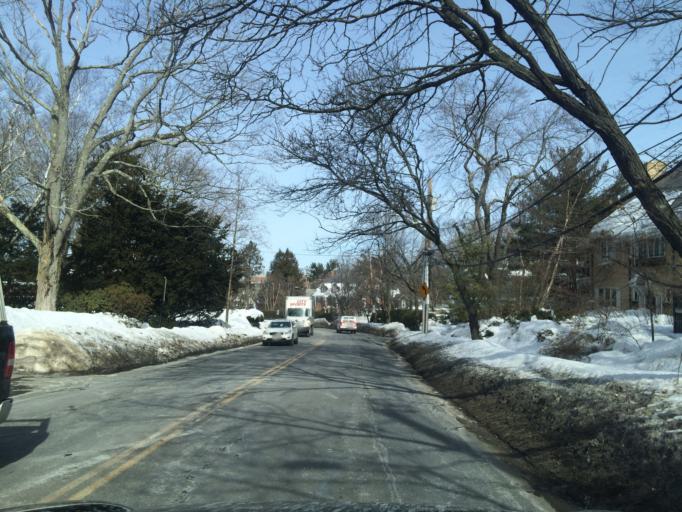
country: US
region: Massachusetts
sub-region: Norfolk County
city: Brookline
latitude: 42.3332
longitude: -71.1473
